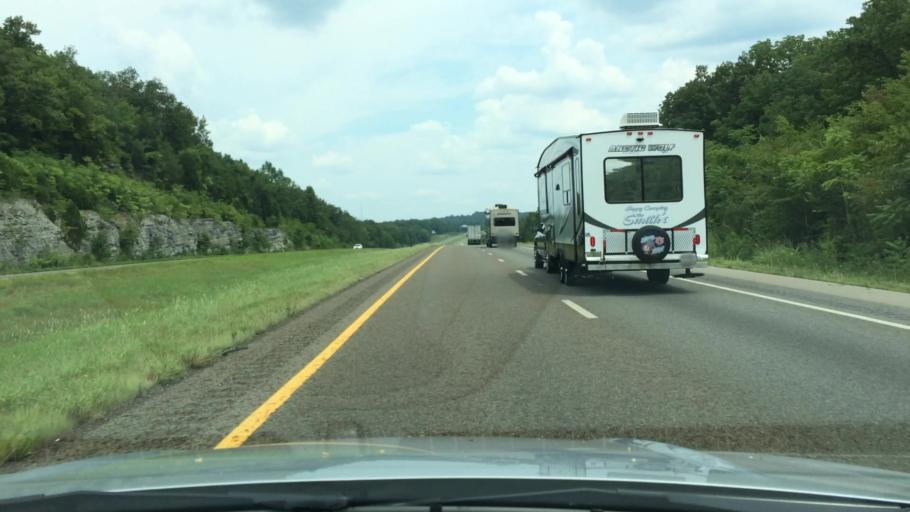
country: US
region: Tennessee
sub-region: Maury County
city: Columbia
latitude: 35.6098
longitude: -86.9006
